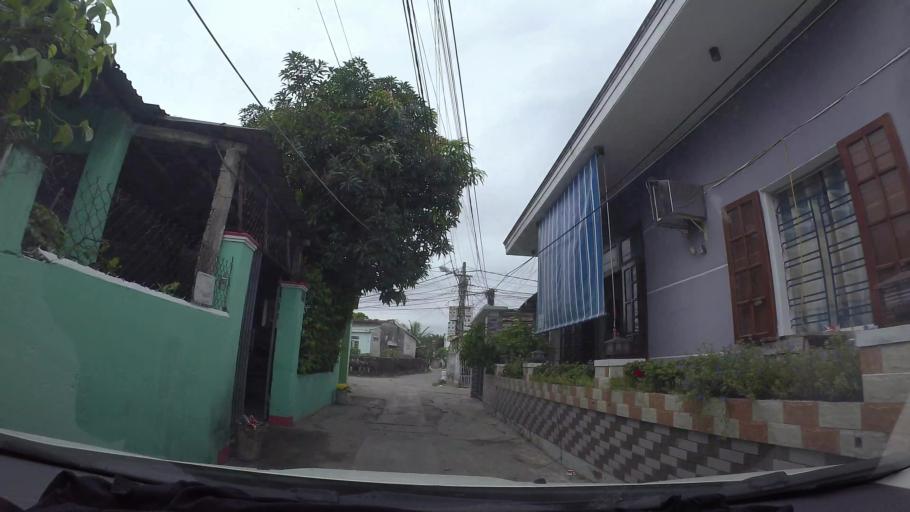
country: VN
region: Da Nang
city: Lien Chieu
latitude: 16.1203
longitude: 108.1168
